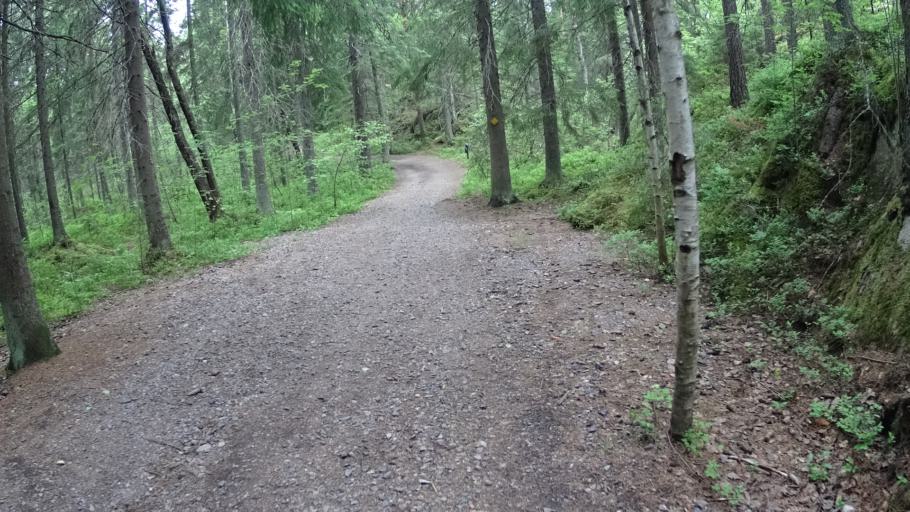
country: FI
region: Uusimaa
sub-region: Helsinki
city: Espoo
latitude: 60.3031
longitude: 24.5098
